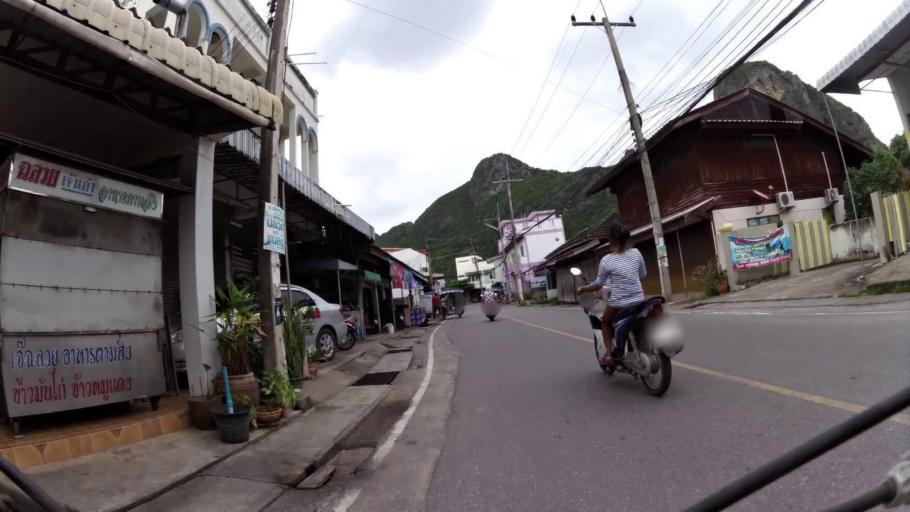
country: TH
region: Prachuap Khiri Khan
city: Prachuap Khiri Khan
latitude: 11.7458
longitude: 99.7901
